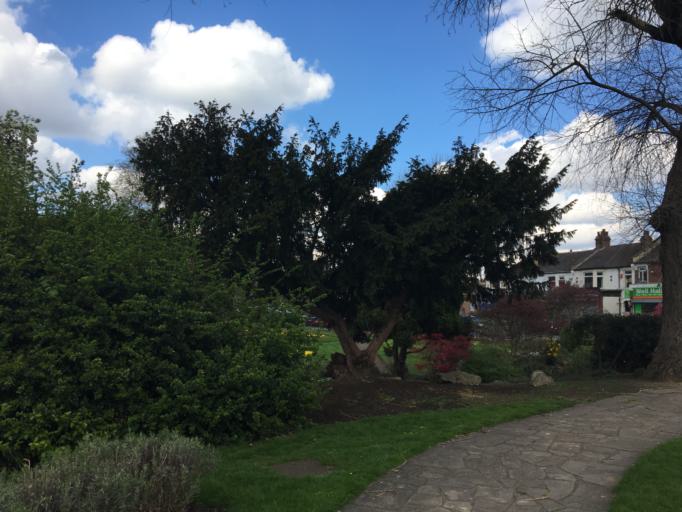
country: GB
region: England
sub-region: Greater London
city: Woolwich
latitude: 51.4558
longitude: 0.0504
